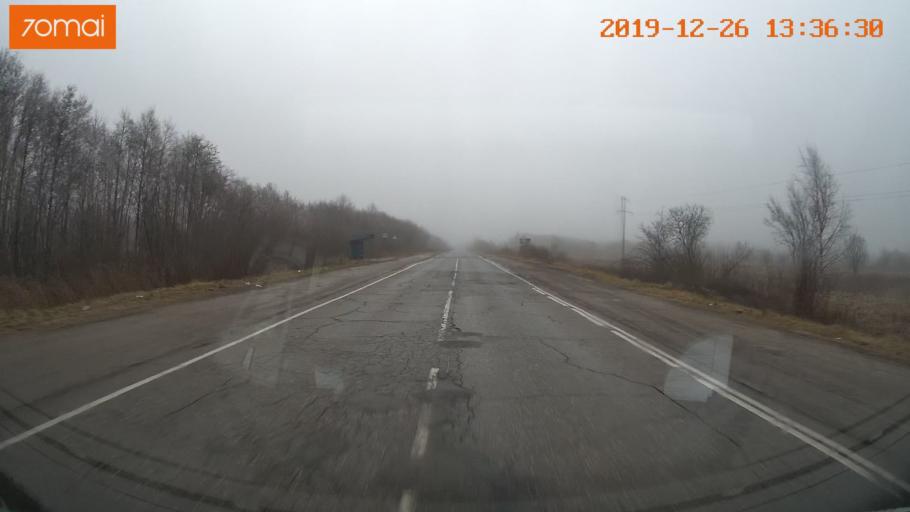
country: RU
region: Vologda
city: Sheksna
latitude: 58.7818
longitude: 38.3562
